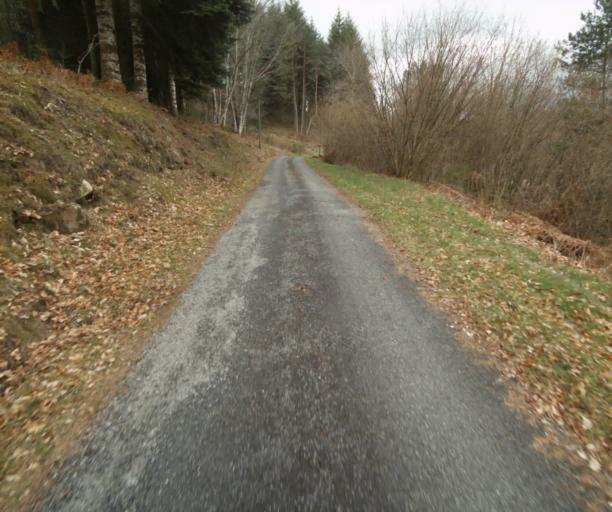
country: FR
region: Limousin
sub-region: Departement de la Correze
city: Correze
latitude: 45.2643
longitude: 1.9578
